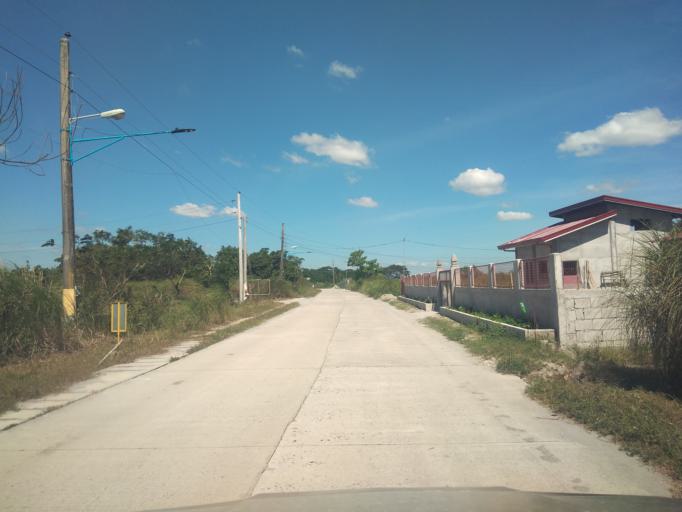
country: PH
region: Central Luzon
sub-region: Province of Pampanga
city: Balas
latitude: 15.0483
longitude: 120.6123
